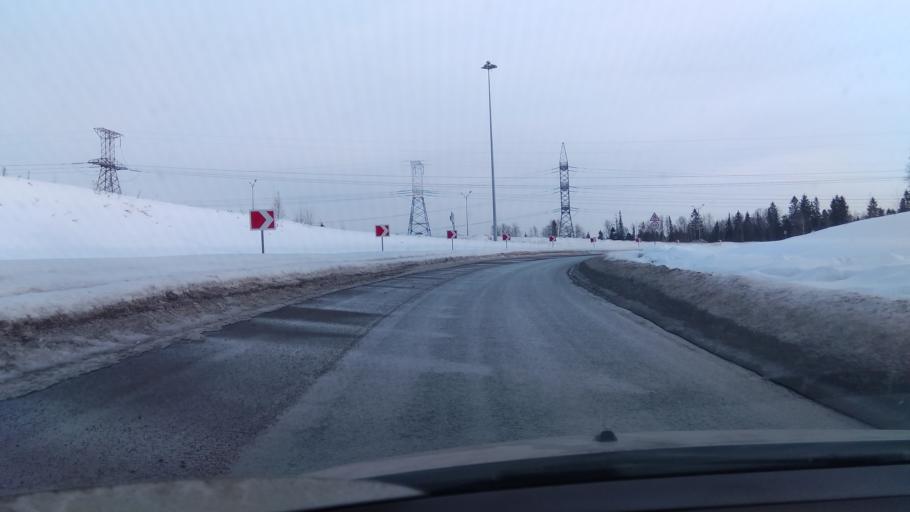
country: RU
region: Perm
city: Ferma
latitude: 57.9987
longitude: 56.3830
